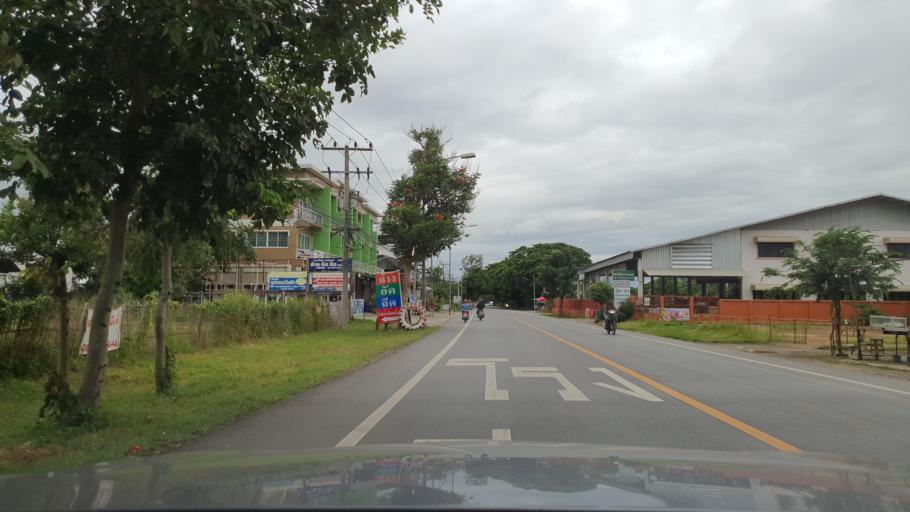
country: TH
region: Lamphun
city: Lamphun
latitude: 18.5923
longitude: 98.9776
